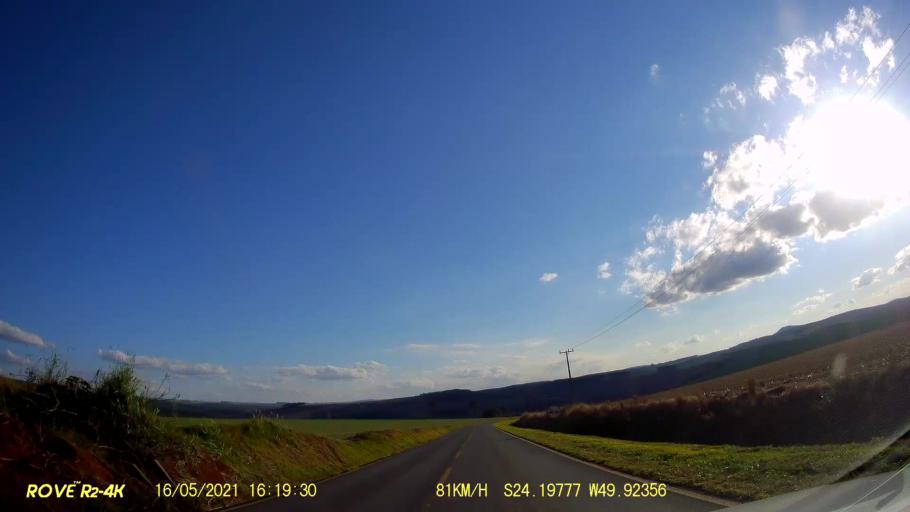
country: BR
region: Parana
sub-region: Jaguariaiva
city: Jaguariaiva
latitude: -24.1978
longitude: -49.9238
